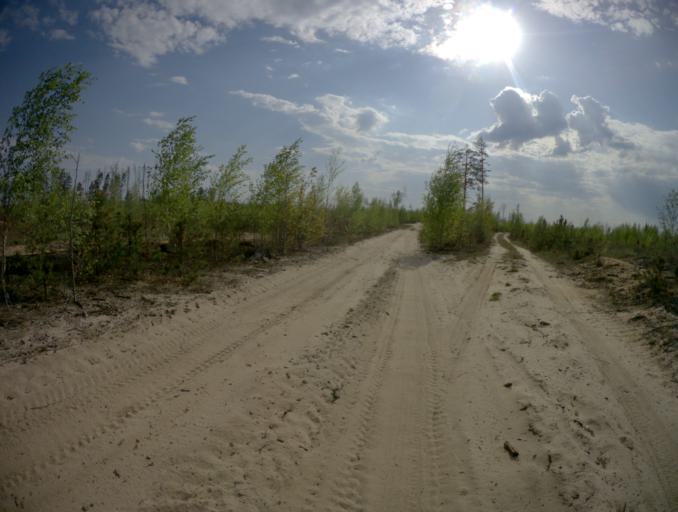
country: RU
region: Ivanovo
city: Talitsy
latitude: 56.4211
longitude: 42.2800
